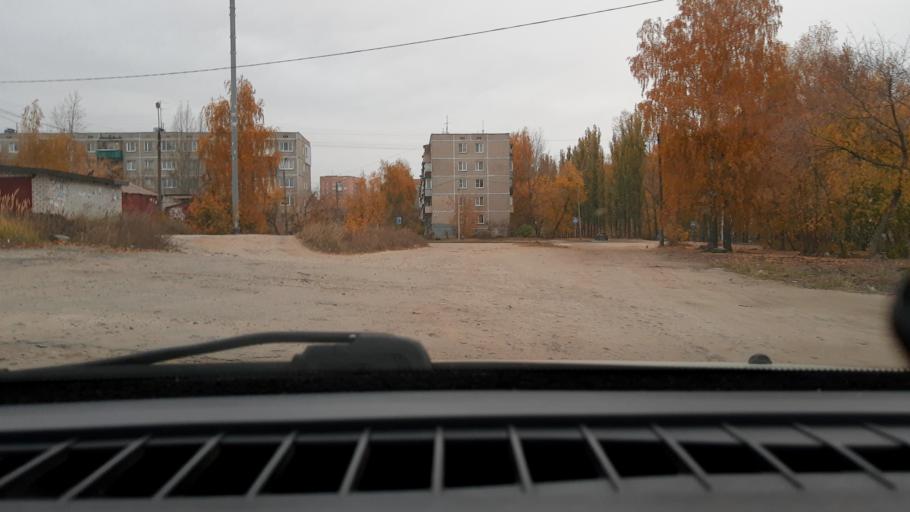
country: RU
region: Nizjnij Novgorod
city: Gorbatovka
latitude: 56.3545
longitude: 43.8191
